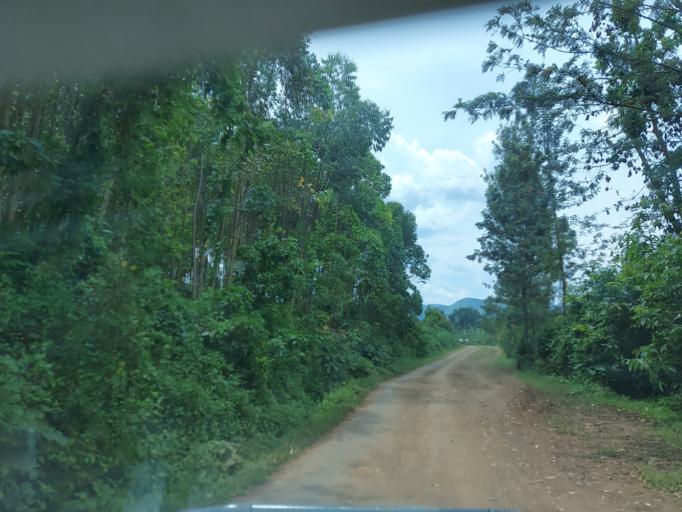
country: CD
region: South Kivu
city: Bukavu
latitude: -2.2455
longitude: 28.8205
